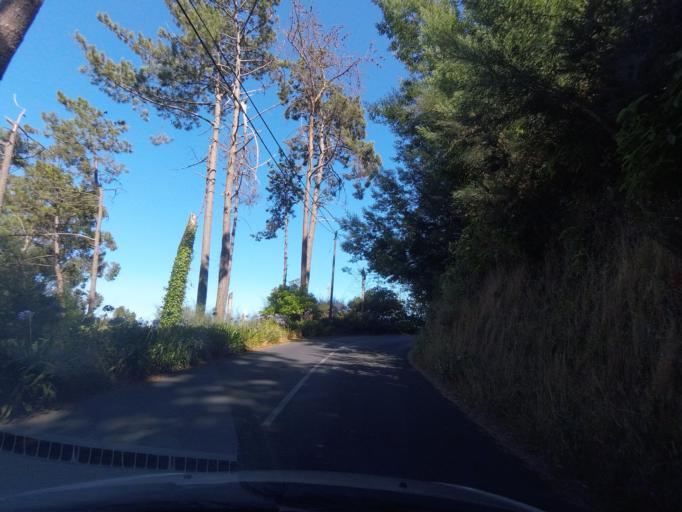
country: PT
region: Madeira
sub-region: Santa Cruz
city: Camacha
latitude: 32.6893
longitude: -16.8522
